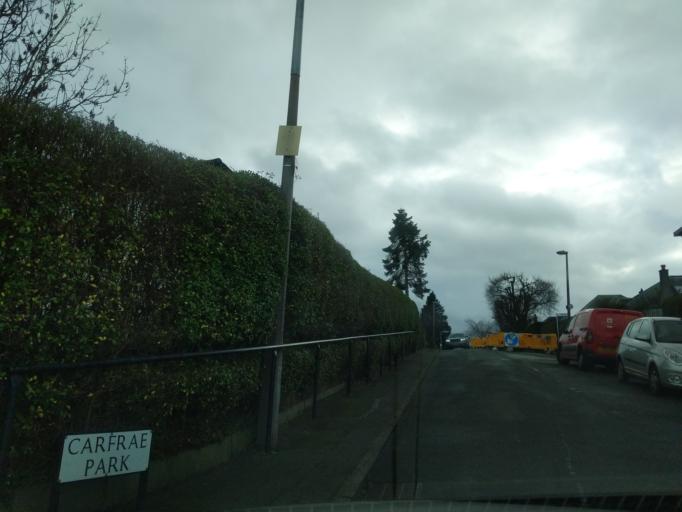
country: GB
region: Scotland
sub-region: Edinburgh
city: Colinton
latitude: 55.9599
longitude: -3.2648
